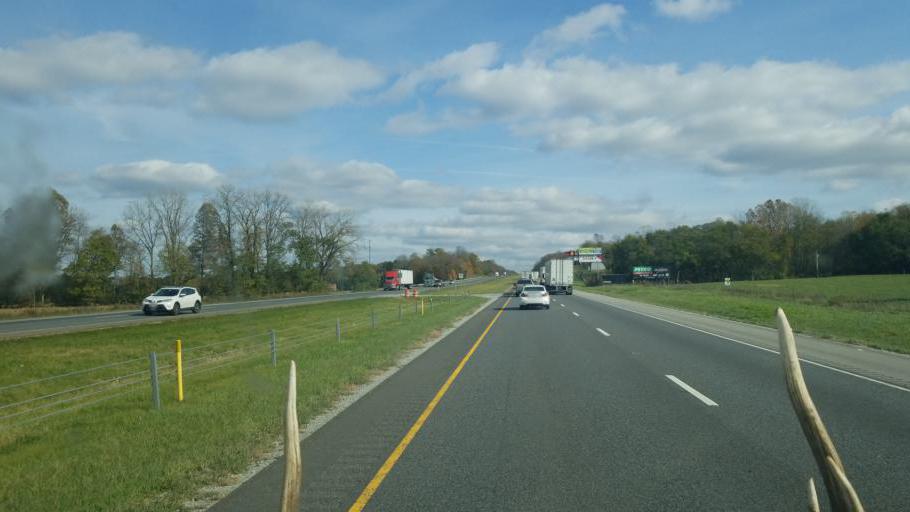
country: US
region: Indiana
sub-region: Henry County
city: Knightstown
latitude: 39.8534
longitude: -85.4737
